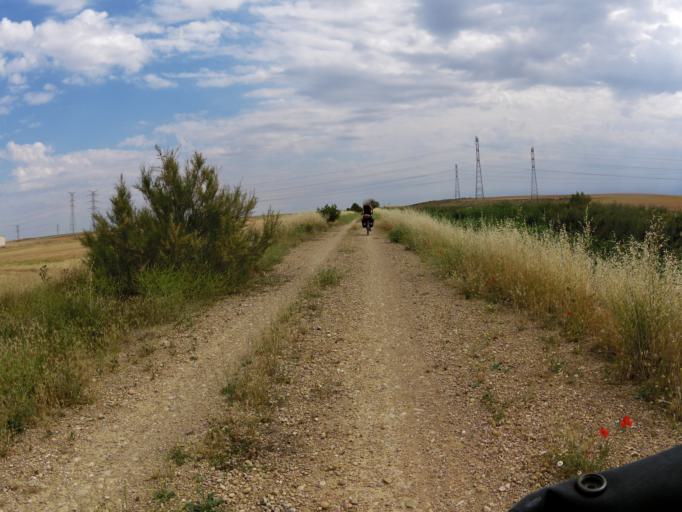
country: ES
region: Castille-La Mancha
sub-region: Provincia de Albacete
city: Albacete
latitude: 39.0322
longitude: -1.7910
